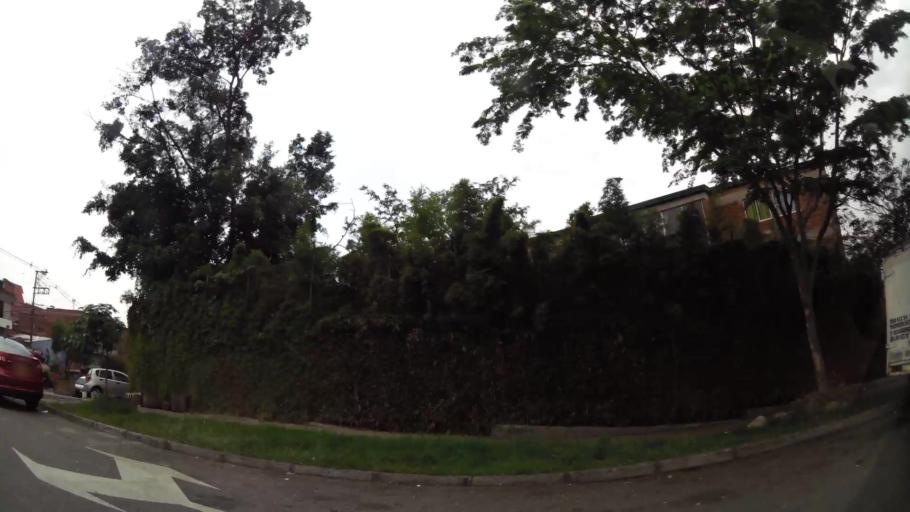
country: CO
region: Antioquia
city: Medellin
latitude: 6.2325
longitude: -75.5528
